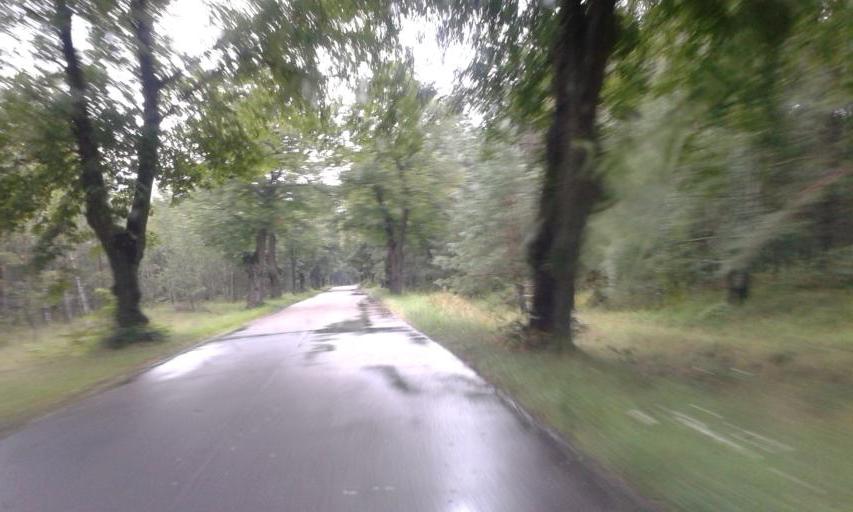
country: PL
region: West Pomeranian Voivodeship
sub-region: Powiat szczecinecki
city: Borne Sulinowo
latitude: 53.5086
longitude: 16.4963
